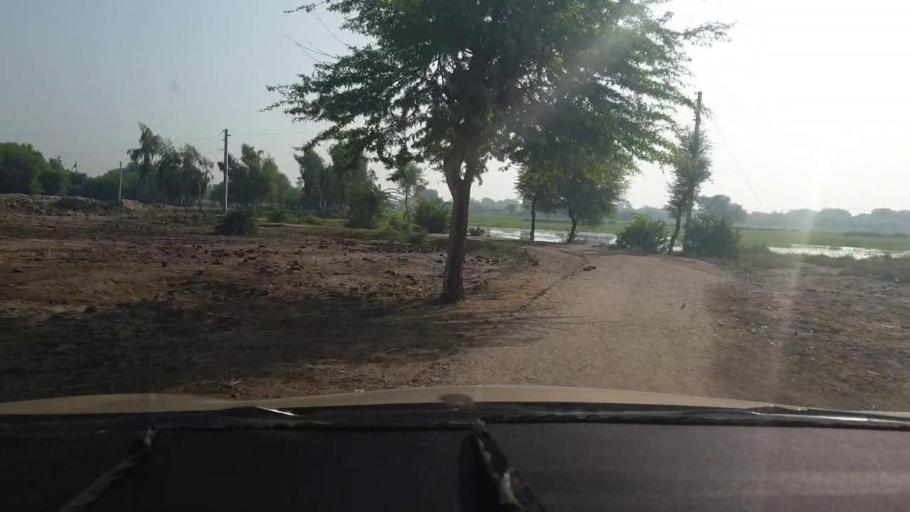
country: PK
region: Sindh
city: Kambar
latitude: 27.6020
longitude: 68.1122
